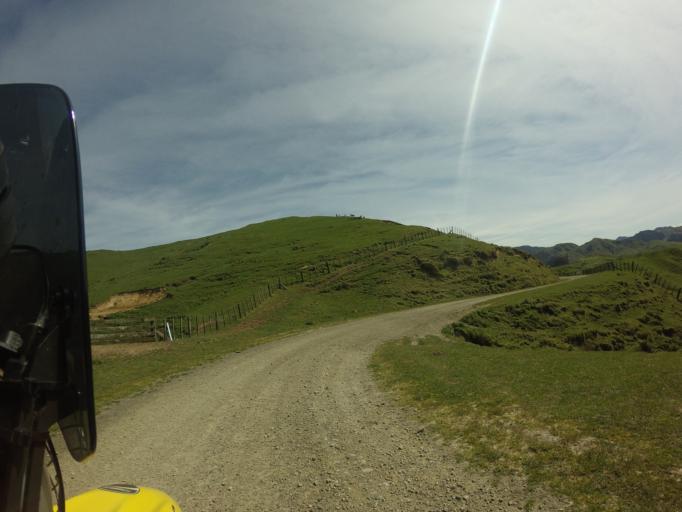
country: NZ
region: Bay of Plenty
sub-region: Opotiki District
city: Opotiki
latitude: -38.4544
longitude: 177.3594
